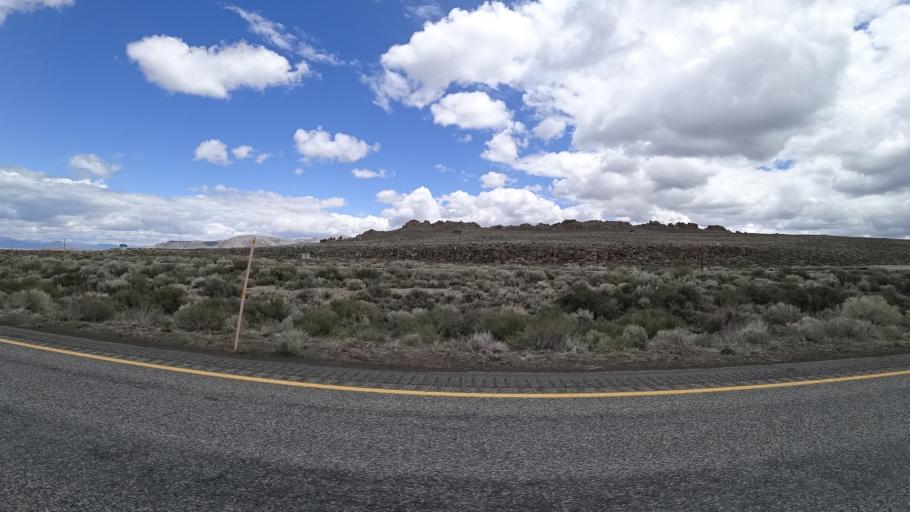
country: US
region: California
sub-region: Mono County
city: Mammoth Lakes
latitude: 37.8627
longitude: -119.0868
